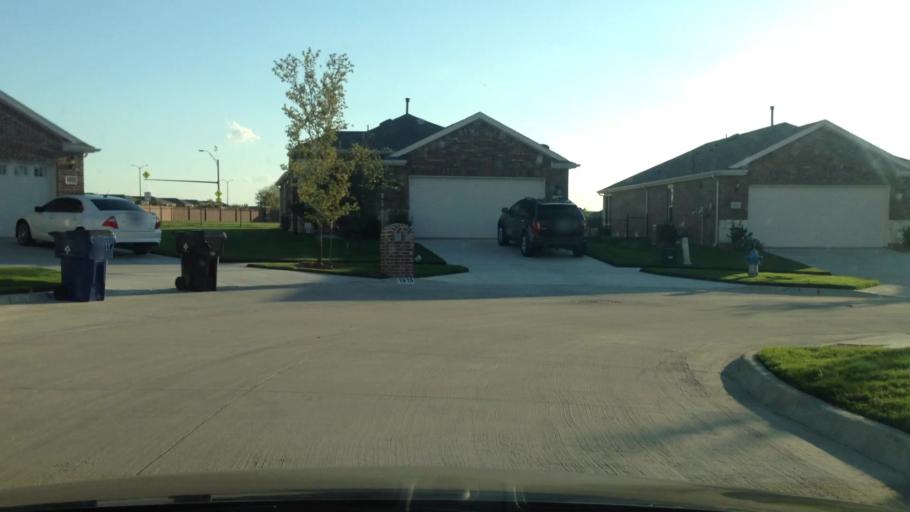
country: US
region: Texas
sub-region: Denton County
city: Little Elm
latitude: 33.1445
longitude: -96.9089
